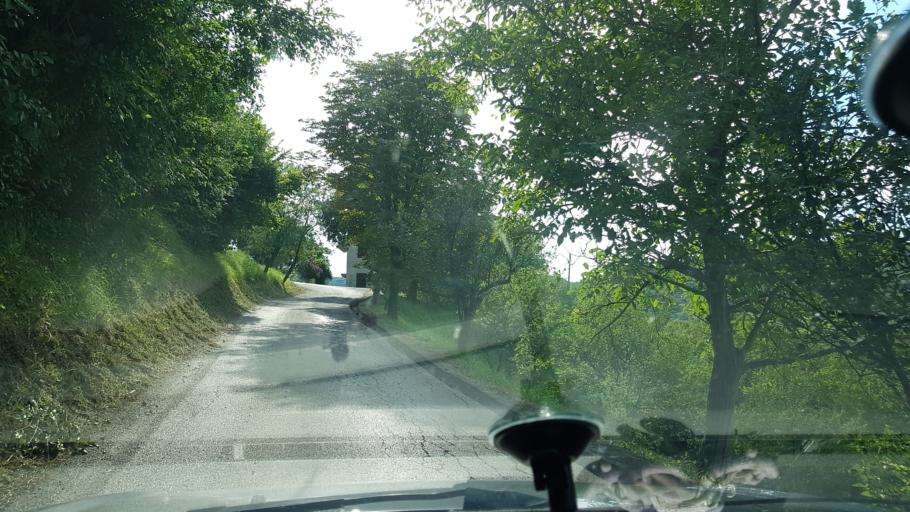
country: SI
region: Koper-Capodistria
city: Koper
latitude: 45.5312
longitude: 13.7136
